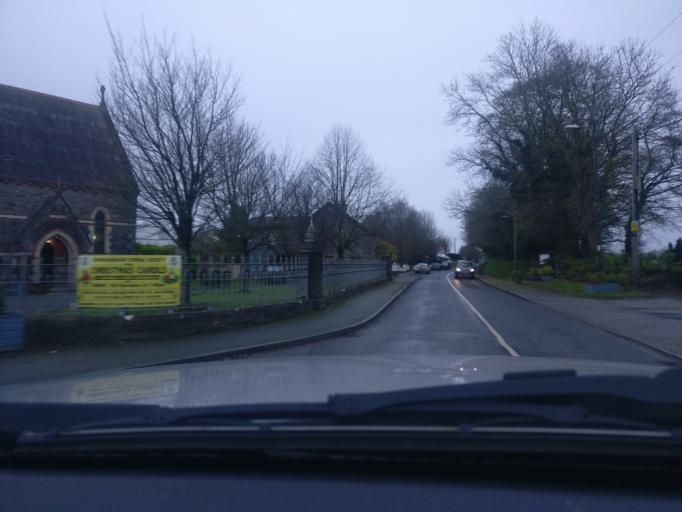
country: IE
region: Leinster
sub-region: An Mhi
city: Dunshaughlin
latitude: 53.4906
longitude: -6.6064
